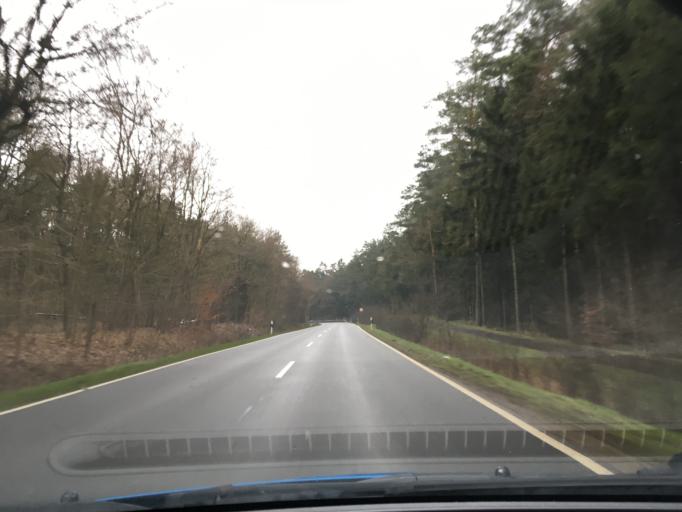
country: DE
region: Schleswig-Holstein
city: Roseburg
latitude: 53.5415
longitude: 10.6369
